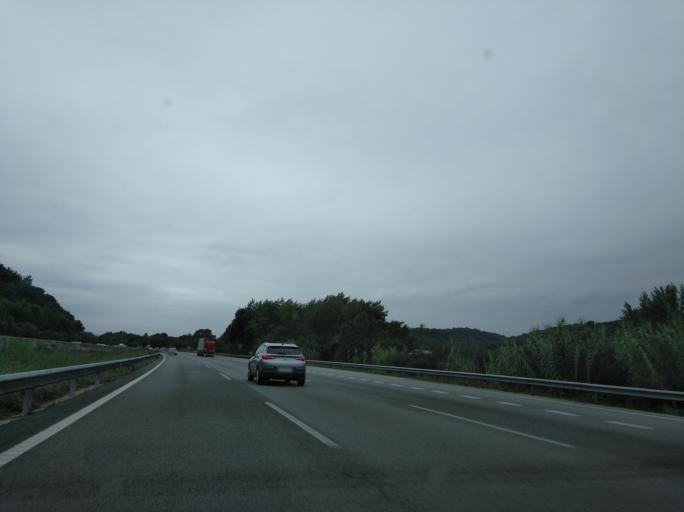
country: ES
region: Catalonia
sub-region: Provincia de Barcelona
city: Sant Celoni
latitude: 41.7046
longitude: 2.5230
